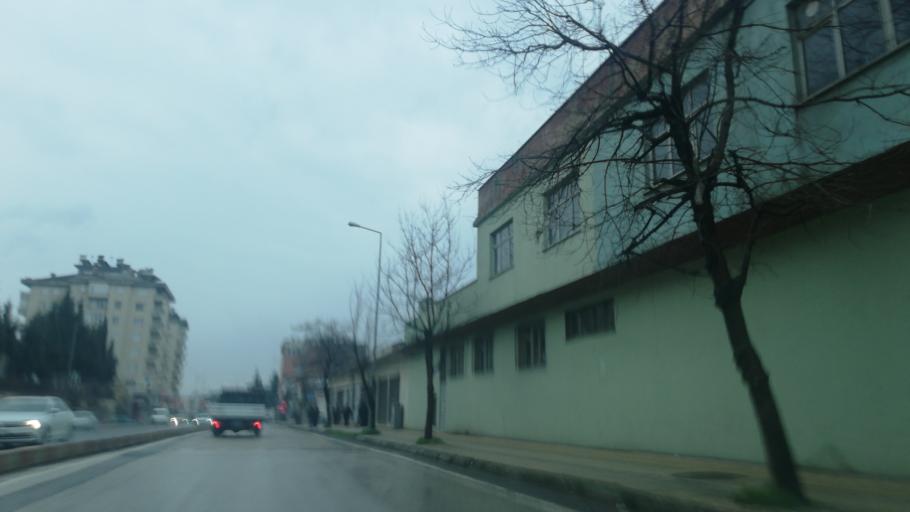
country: TR
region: Kahramanmaras
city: Kahramanmaras
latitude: 37.5731
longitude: 36.9395
